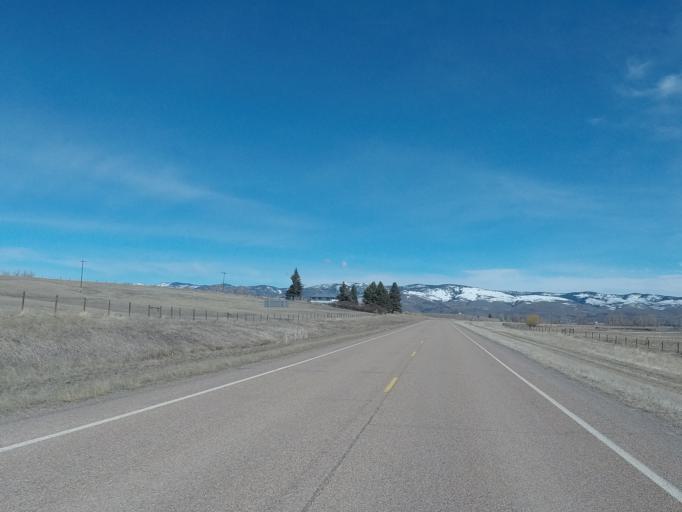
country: US
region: Montana
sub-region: Granite County
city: Philipsburg
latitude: 46.6033
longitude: -113.1863
